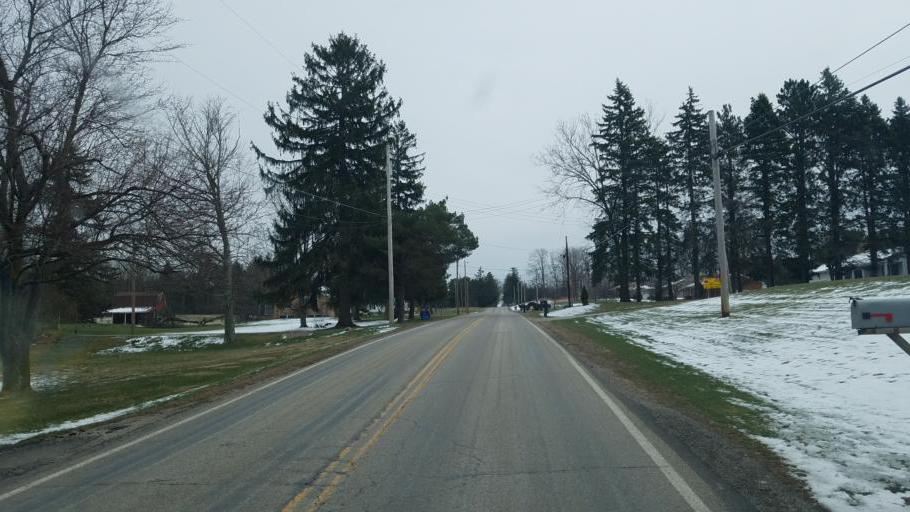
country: US
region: Ohio
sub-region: Richland County
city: Ontario
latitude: 40.7467
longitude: -82.6211
